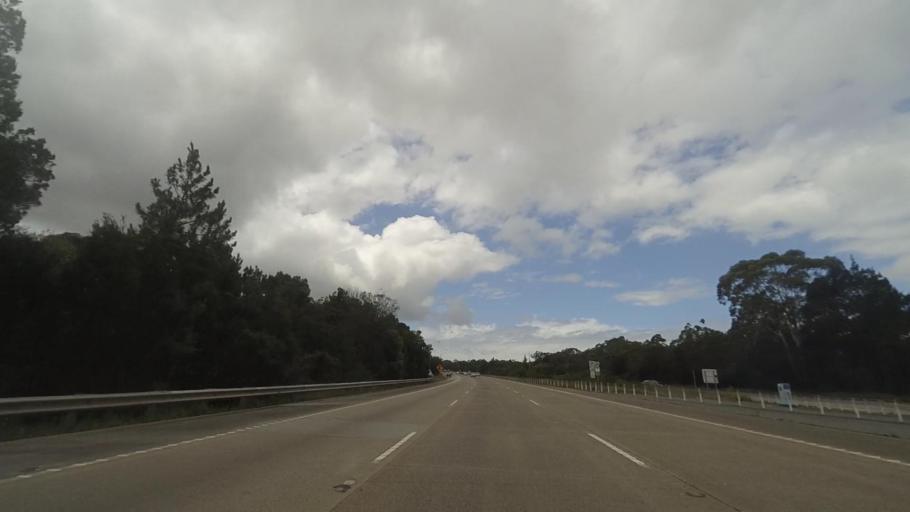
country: AU
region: New South Wales
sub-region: Gosford Shire
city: Point Clare
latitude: -33.4205
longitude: 151.2910
